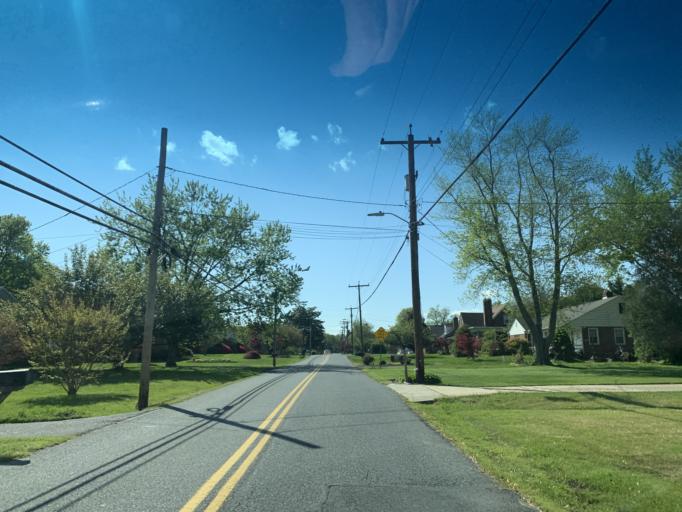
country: US
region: Maryland
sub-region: Harford County
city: Riverside
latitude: 39.4566
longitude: -76.2517
